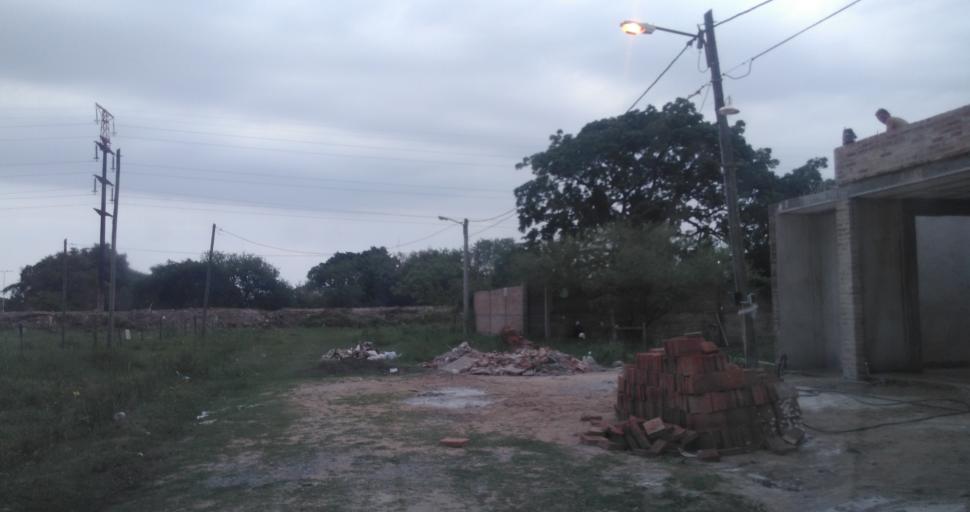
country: AR
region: Chaco
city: Resistencia
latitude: -27.4345
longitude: -58.9636
